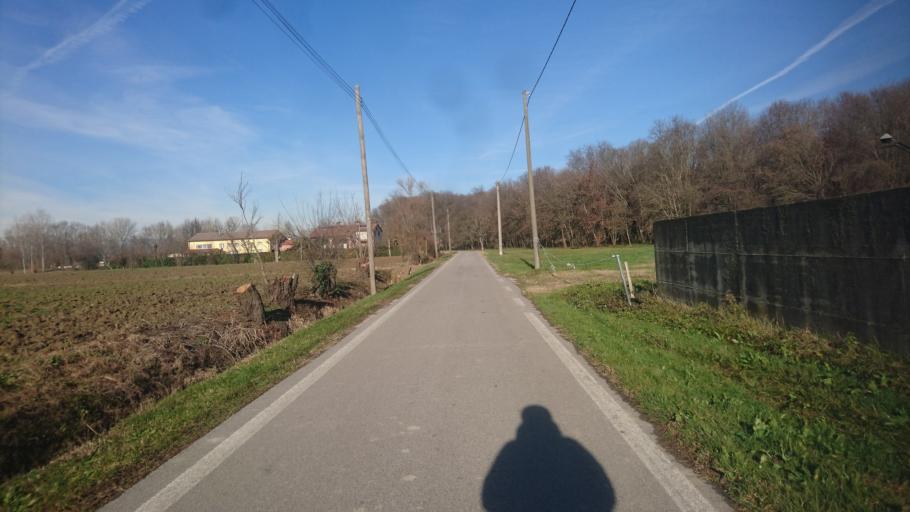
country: IT
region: Veneto
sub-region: Provincia di Padova
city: Piazzola sul Brenta
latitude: 45.5193
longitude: 11.7782
